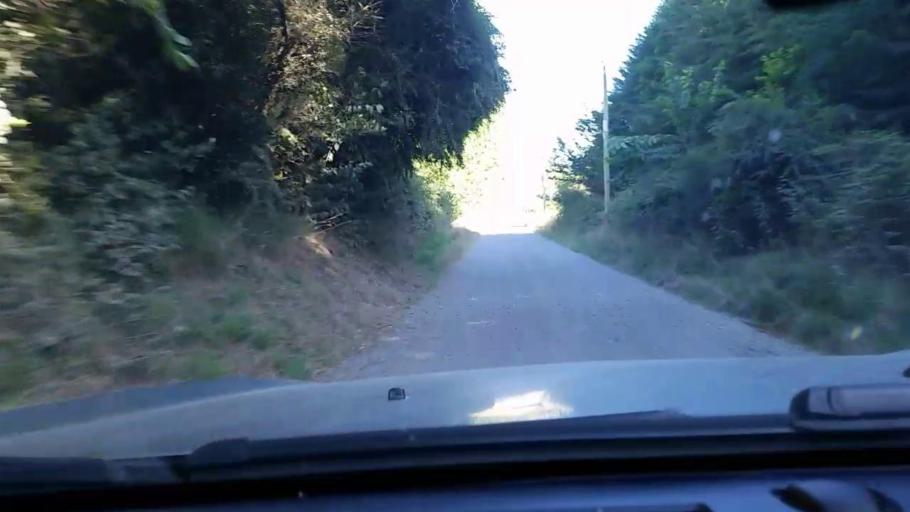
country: NZ
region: Bay of Plenty
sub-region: Rotorua District
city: Rotorua
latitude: -38.3950
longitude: 176.1737
